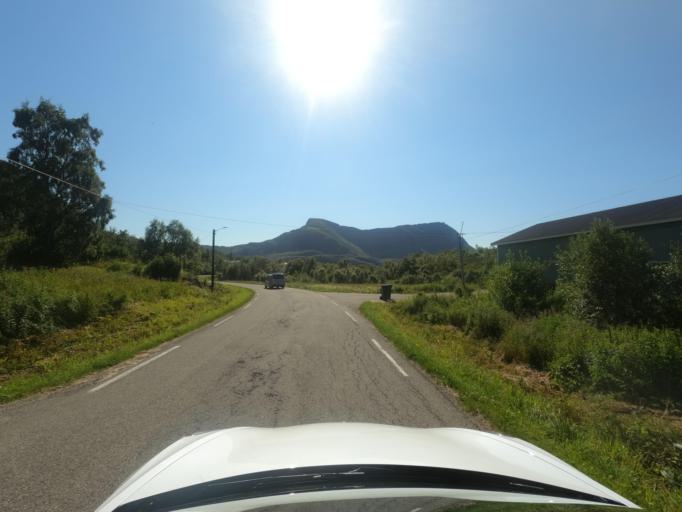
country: NO
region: Nordland
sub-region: Hadsel
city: Stokmarknes
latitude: 68.3087
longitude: 14.9937
